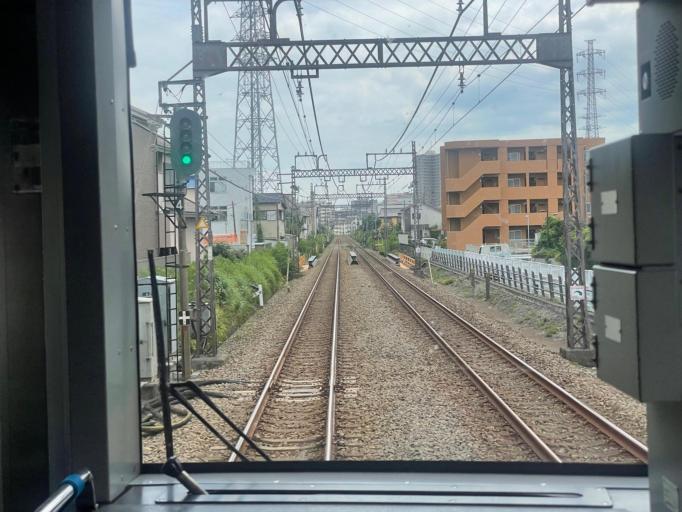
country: JP
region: Kanagawa
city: Fujisawa
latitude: 35.4055
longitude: 139.4647
